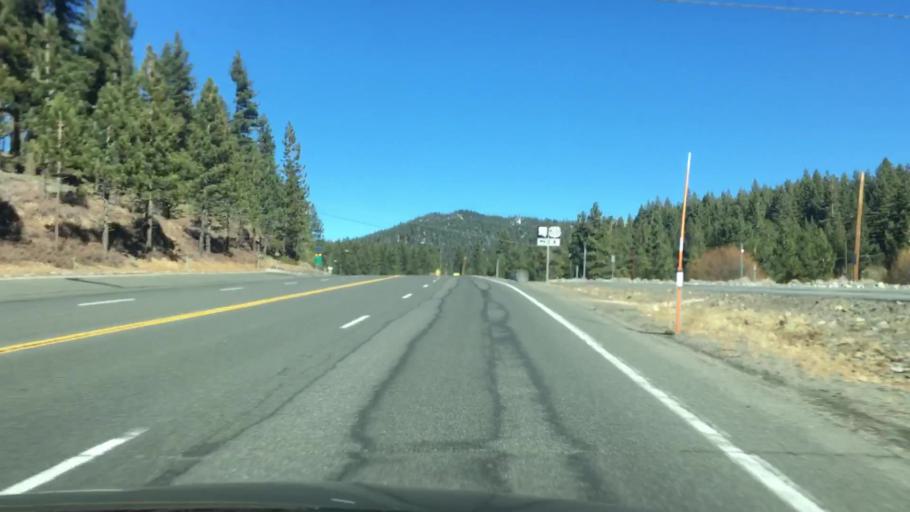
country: US
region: Nevada
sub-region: Douglas County
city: Kingsbury
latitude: 39.0966
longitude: -119.9106
